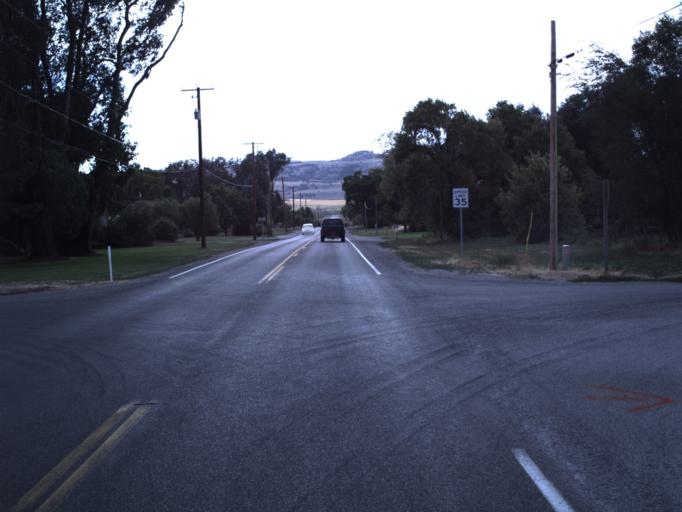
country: US
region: Utah
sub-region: Cache County
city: Benson
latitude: 41.8625
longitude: -111.9910
